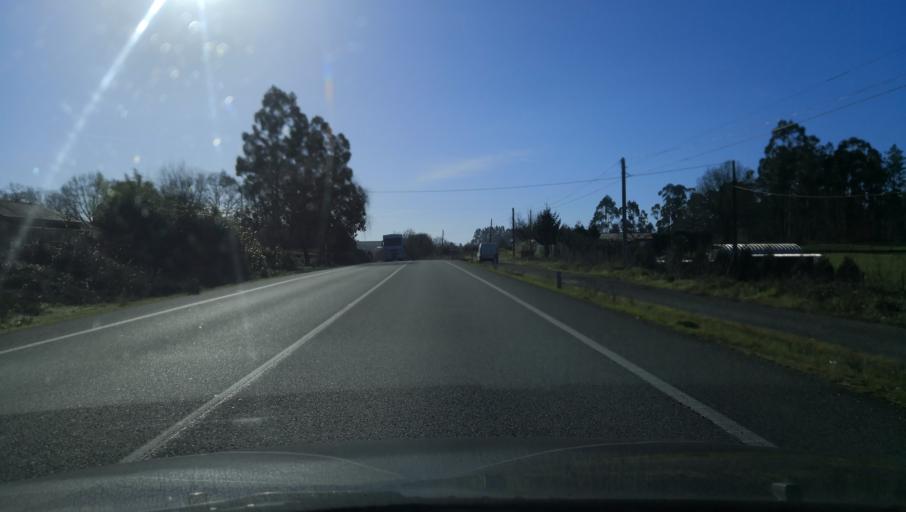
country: ES
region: Galicia
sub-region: Provincia da Coruna
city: Vedra
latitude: 42.8097
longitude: -8.4797
